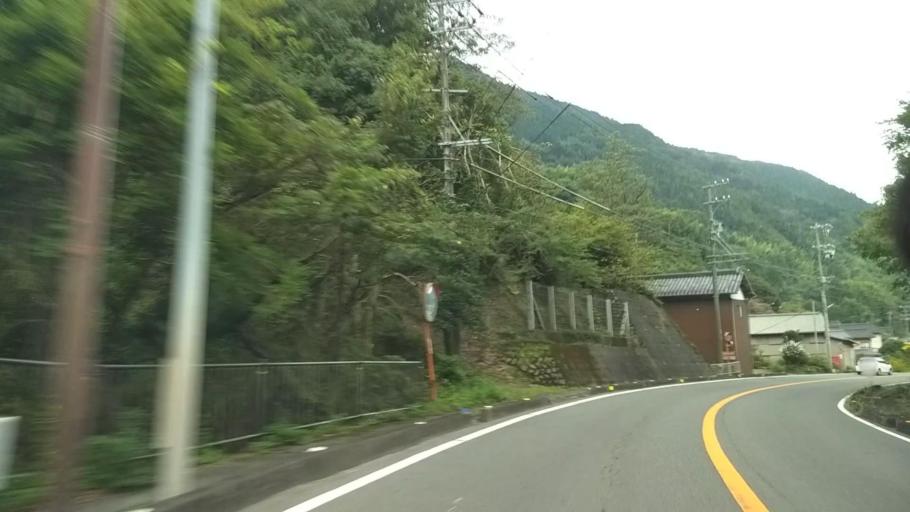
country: JP
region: Shizuoka
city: Fujinomiya
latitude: 35.1357
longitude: 138.5214
